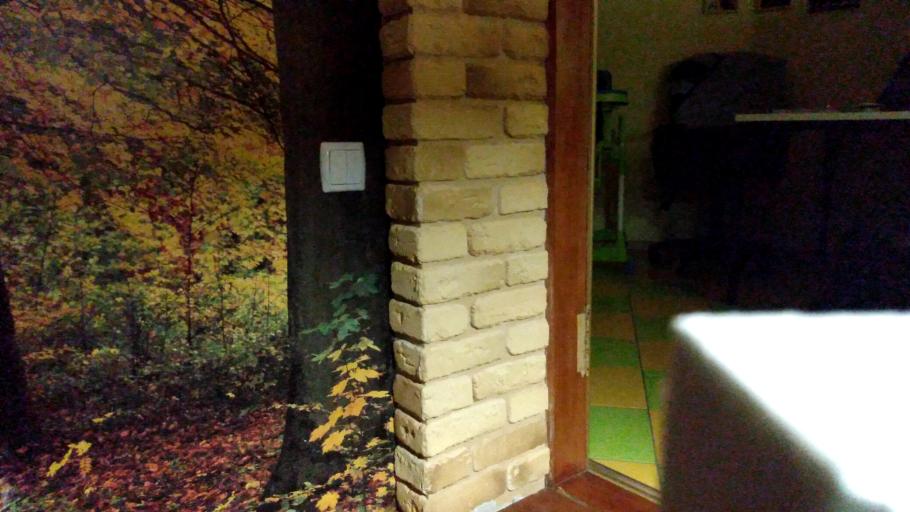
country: RU
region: Vologda
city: Lipin Bor
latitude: 61.0301
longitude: 37.9500
